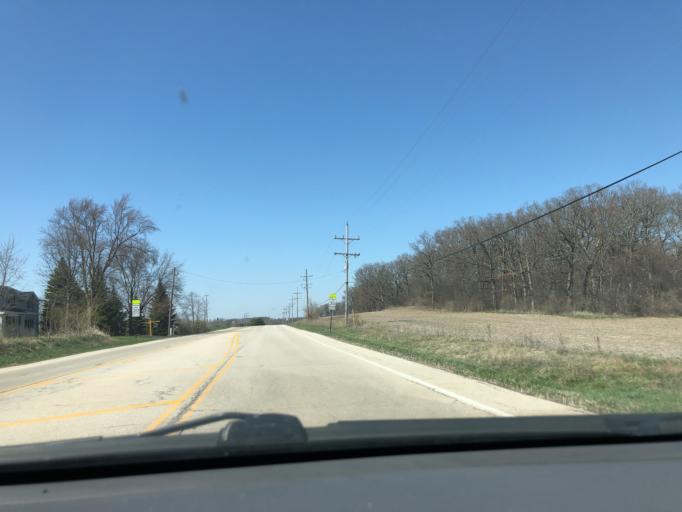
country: US
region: Illinois
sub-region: Kane County
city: Hampshire
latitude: 42.1181
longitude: -88.4912
